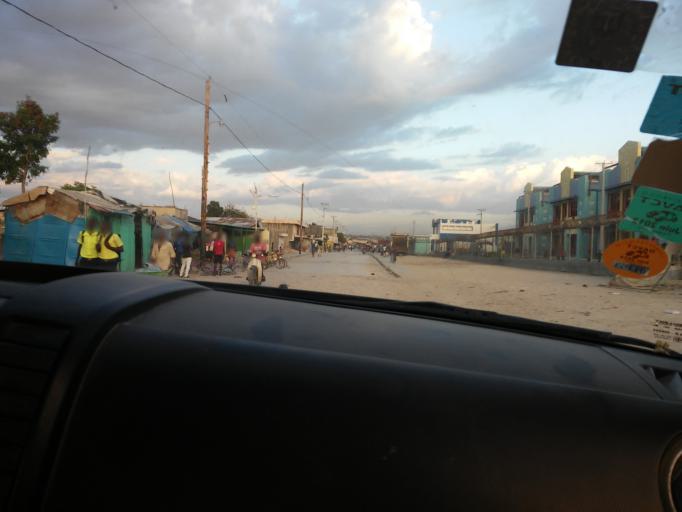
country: HT
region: Ouest
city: Port-au-Prince
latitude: 18.5657
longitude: -72.3498
